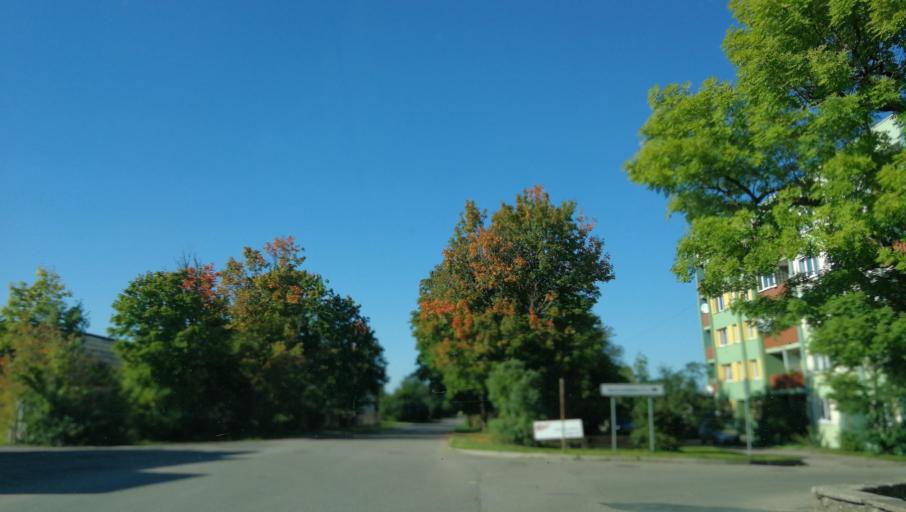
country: LV
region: Aizpute
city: Aizpute
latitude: 56.7232
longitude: 21.5962
